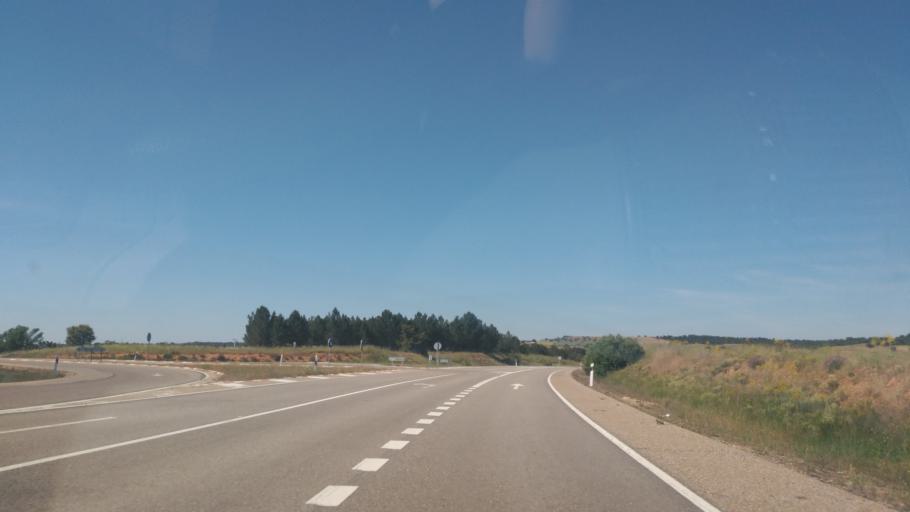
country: ES
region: Castille and Leon
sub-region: Provincia de Zamora
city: Cuelgamures
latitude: 41.2459
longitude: -5.7072
